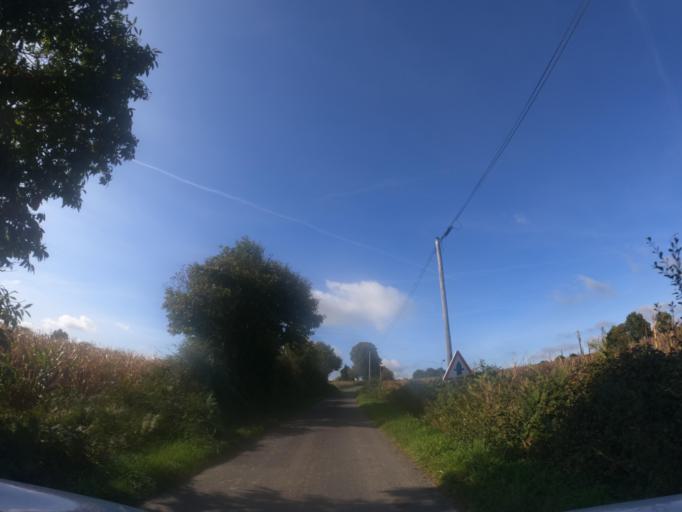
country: FR
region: Poitou-Charentes
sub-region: Departement des Deux-Sevres
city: Courlay
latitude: 46.7897
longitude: -0.5812
